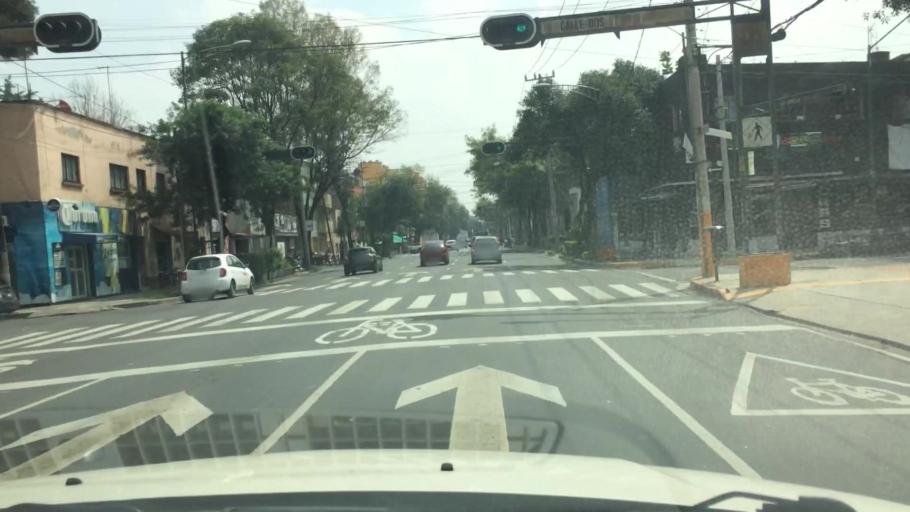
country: MX
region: Mexico City
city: Colonia Nativitas
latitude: 19.3788
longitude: -99.1454
